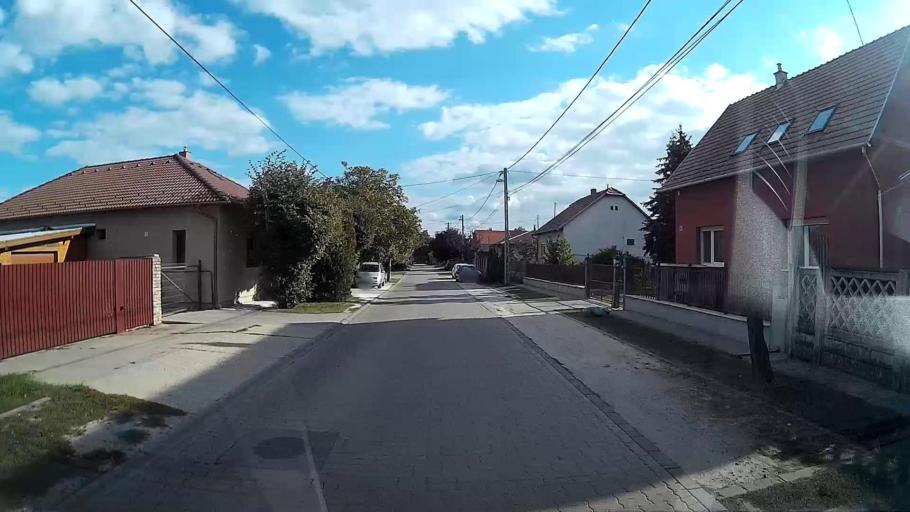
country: HU
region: Pest
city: Pilisvorosvar
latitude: 47.6276
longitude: 18.8993
